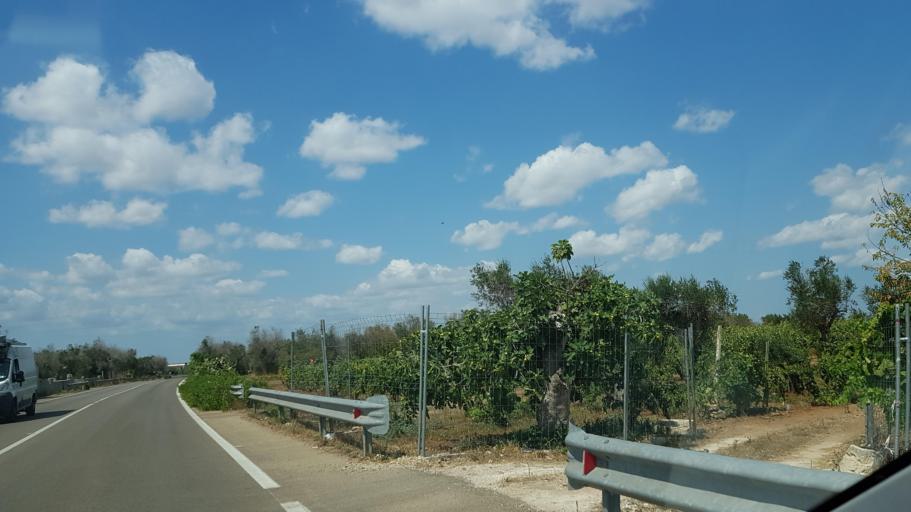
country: IT
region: Apulia
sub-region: Provincia di Lecce
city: Novoli
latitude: 40.3984
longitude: 18.0519
